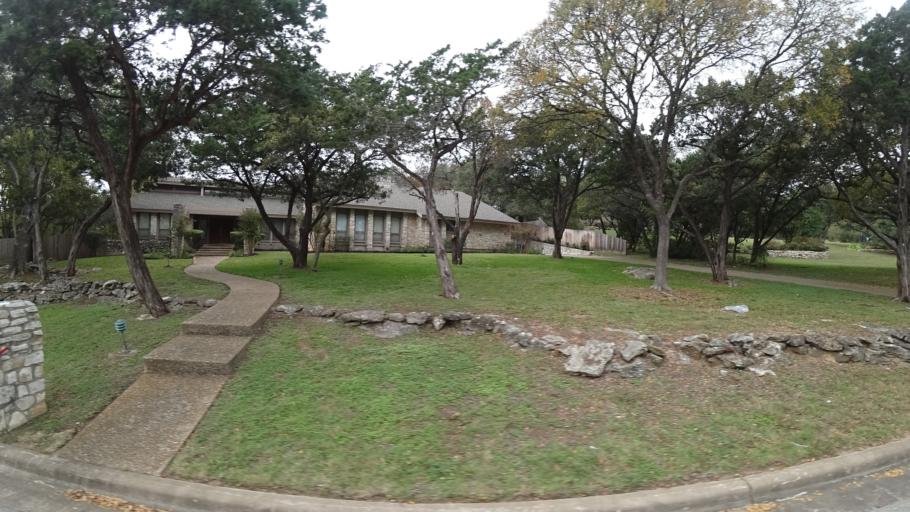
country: US
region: Texas
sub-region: Williamson County
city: Anderson Mill
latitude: 30.4414
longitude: -97.8193
